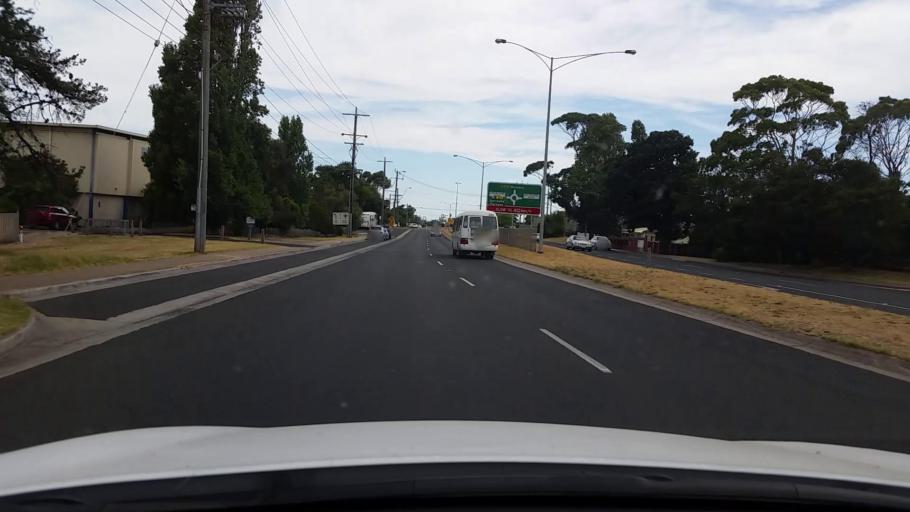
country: AU
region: Victoria
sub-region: Mornington Peninsula
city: Rosebud West
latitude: -38.3697
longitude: 144.8893
